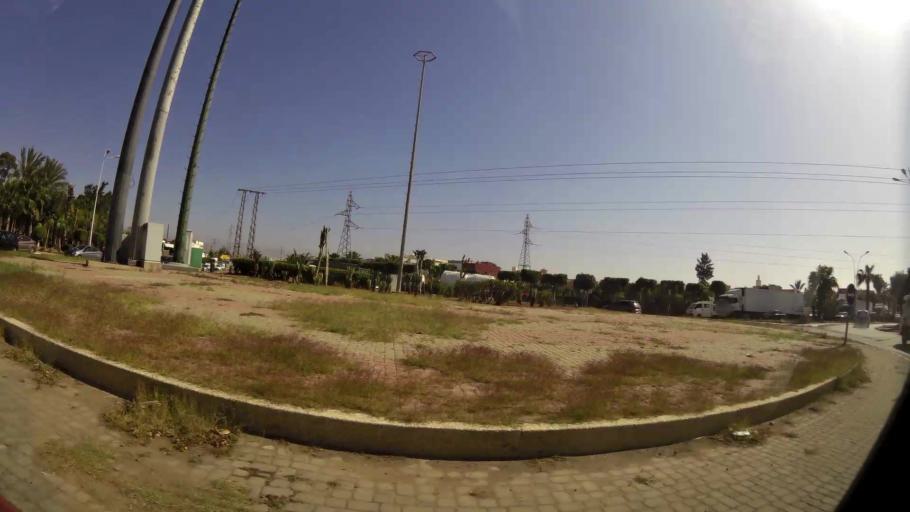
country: MA
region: Souss-Massa-Draa
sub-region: Inezgane-Ait Mellou
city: Inezgane
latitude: 30.3712
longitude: -9.5053
